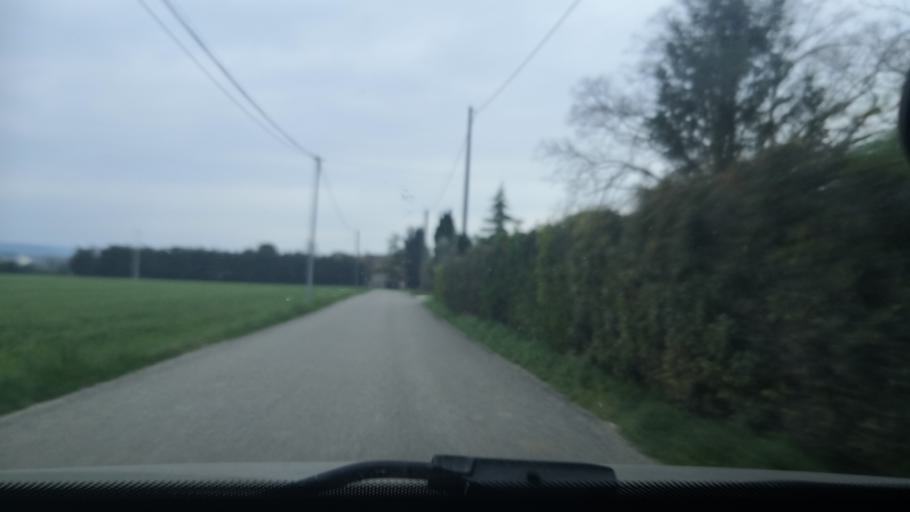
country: FR
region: Rhone-Alpes
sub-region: Departement de la Drome
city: Saint-Marcel-les-Sauzet
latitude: 44.5854
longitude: 4.8190
